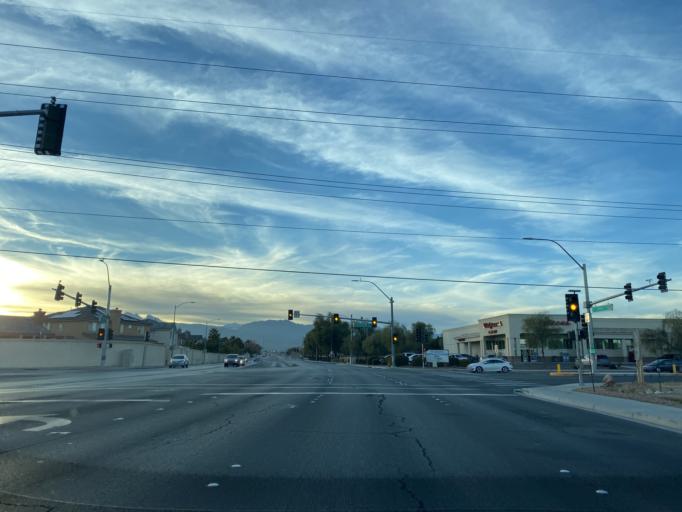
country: US
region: Nevada
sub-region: Clark County
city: Las Vegas
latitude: 36.2632
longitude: -115.2419
